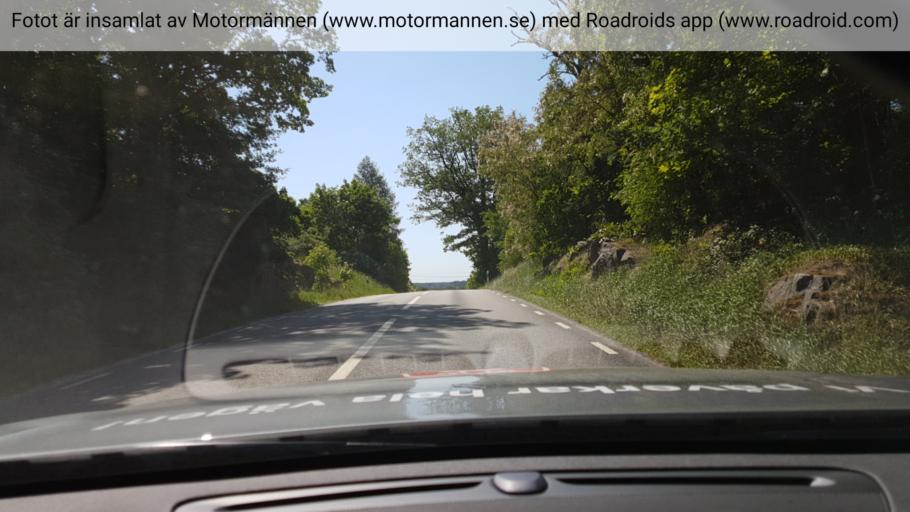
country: SE
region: Stockholm
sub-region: Norrtalje Kommun
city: Rimbo
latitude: 59.7519
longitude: 18.3865
